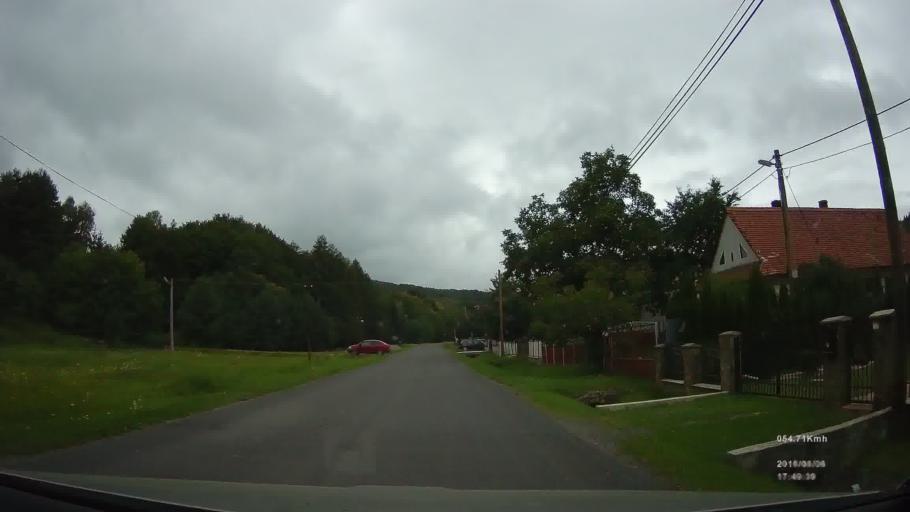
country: SK
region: Presovsky
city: Svidnik
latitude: 49.3850
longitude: 21.5681
